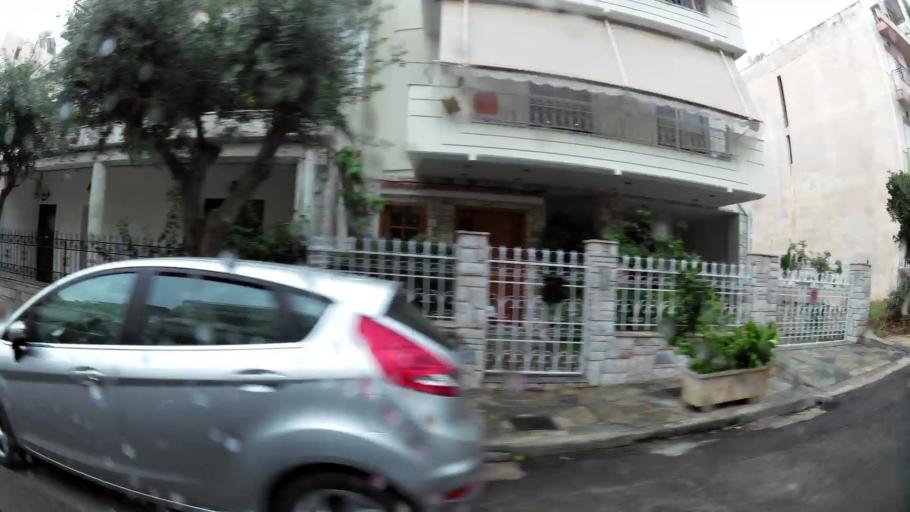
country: GR
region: Attica
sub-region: Nomos Piraios
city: Korydallos
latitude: 37.9861
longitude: 23.6304
